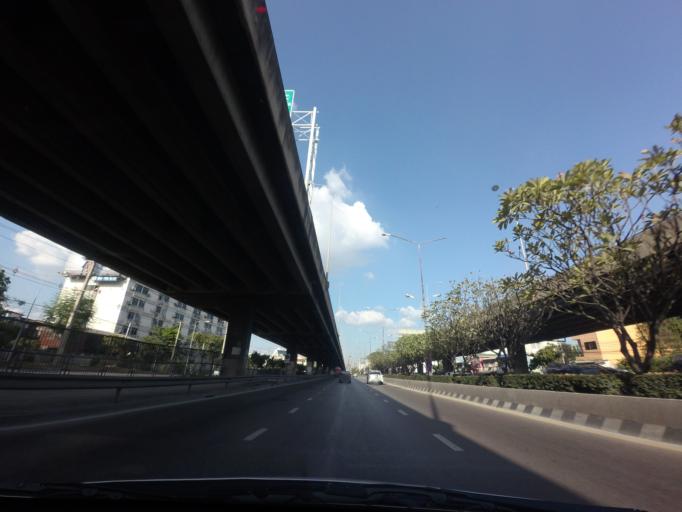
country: TH
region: Bangkok
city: Yan Nawa
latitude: 13.7079
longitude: 100.5487
